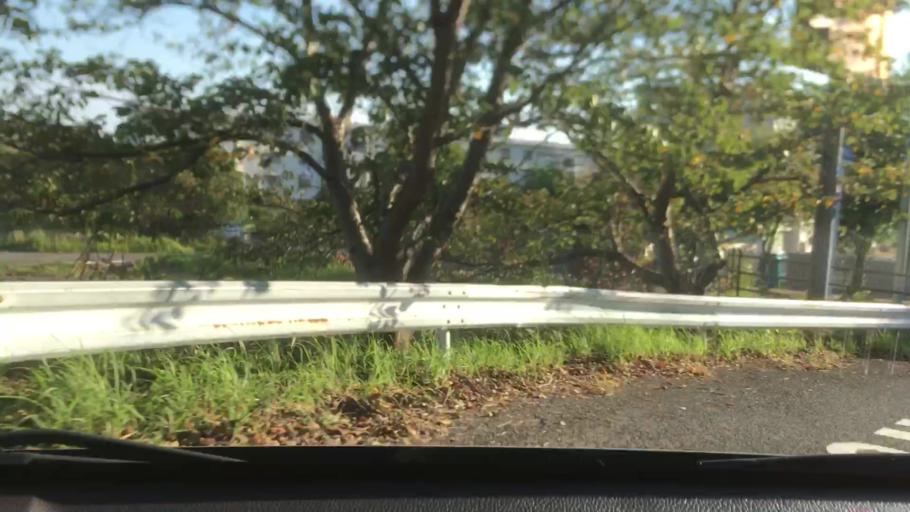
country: JP
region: Nagasaki
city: Sasebo
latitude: 33.0400
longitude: 129.6253
